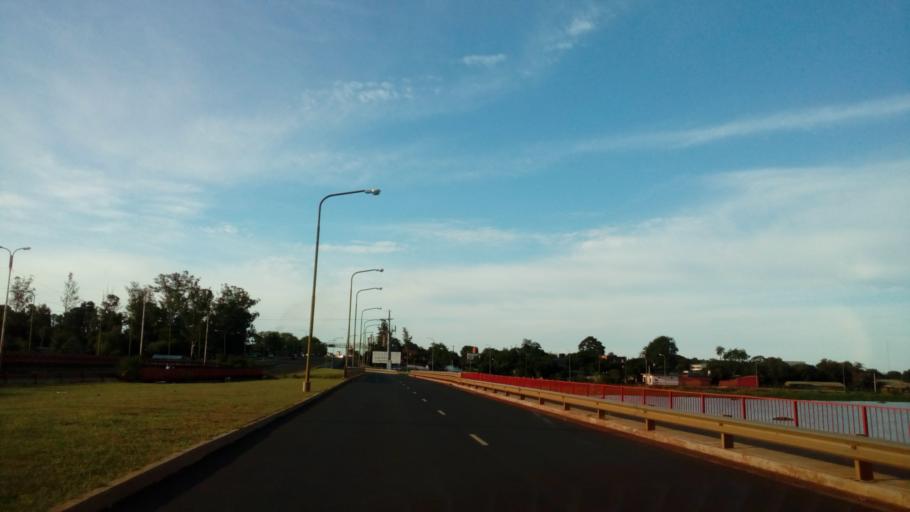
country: AR
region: Misiones
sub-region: Departamento de Capital
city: Posadas
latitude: -27.4195
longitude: -55.8997
